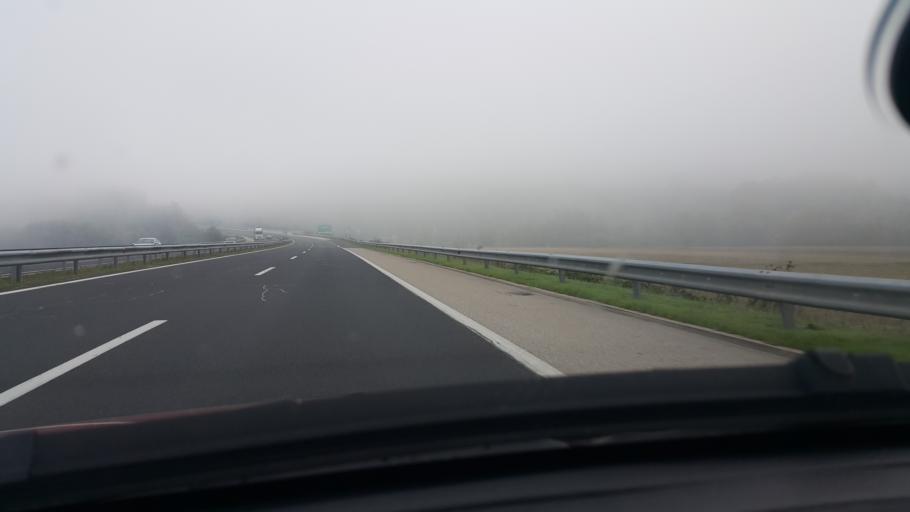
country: SI
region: Brezice
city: Brezice
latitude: 45.8955
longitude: 15.5821
